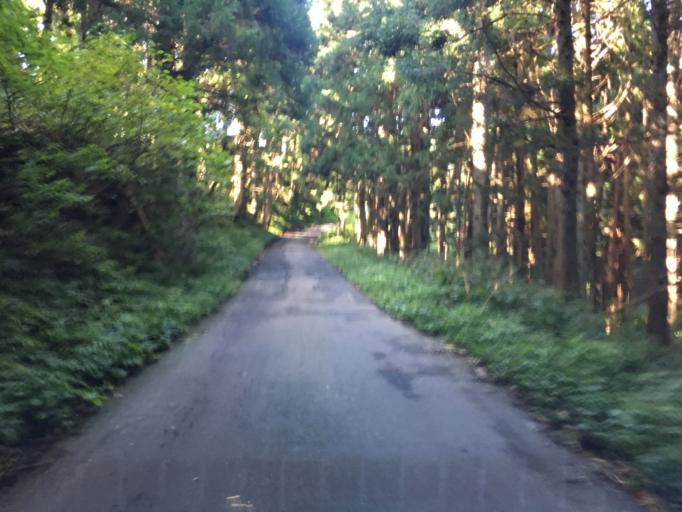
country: JP
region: Yamagata
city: Yonezawa
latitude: 37.8377
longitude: 140.2006
